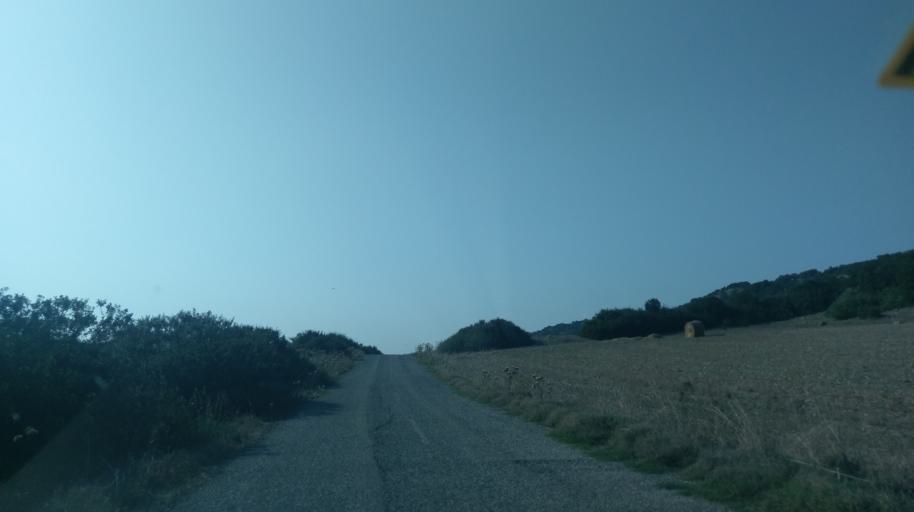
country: CY
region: Ammochostos
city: Rizokarpaso
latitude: 35.5518
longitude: 34.3594
